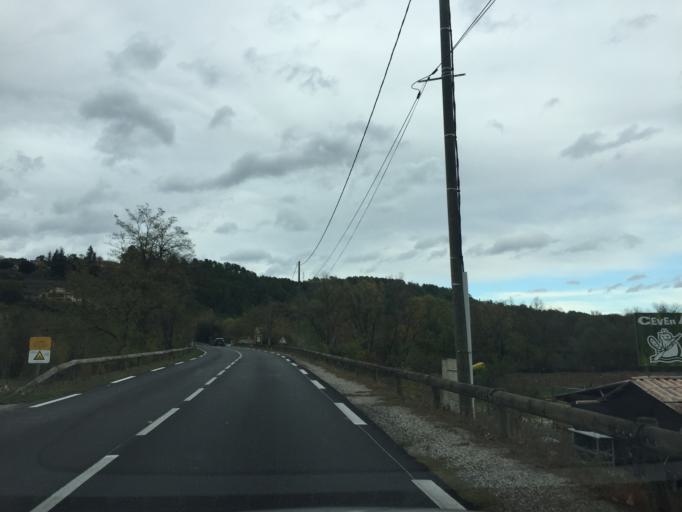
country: FR
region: Rhone-Alpes
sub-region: Departement de l'Ardeche
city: Les Vans
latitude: 44.4148
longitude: 4.1539
